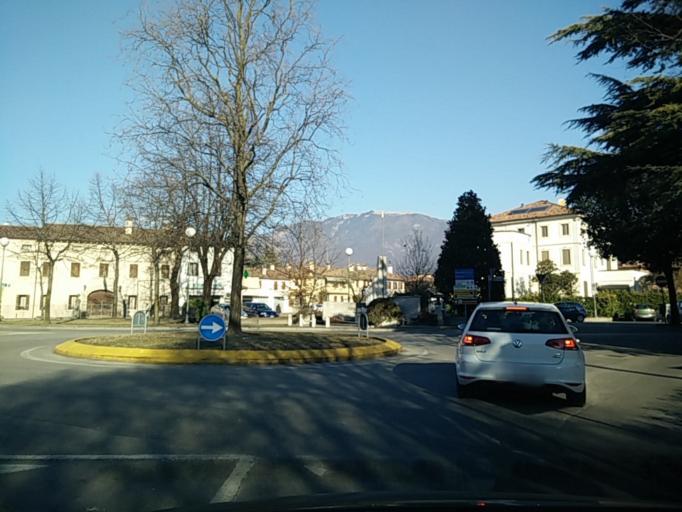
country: IT
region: Veneto
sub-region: Provincia di Treviso
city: Cappella Maggiore
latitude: 45.9690
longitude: 12.3627
